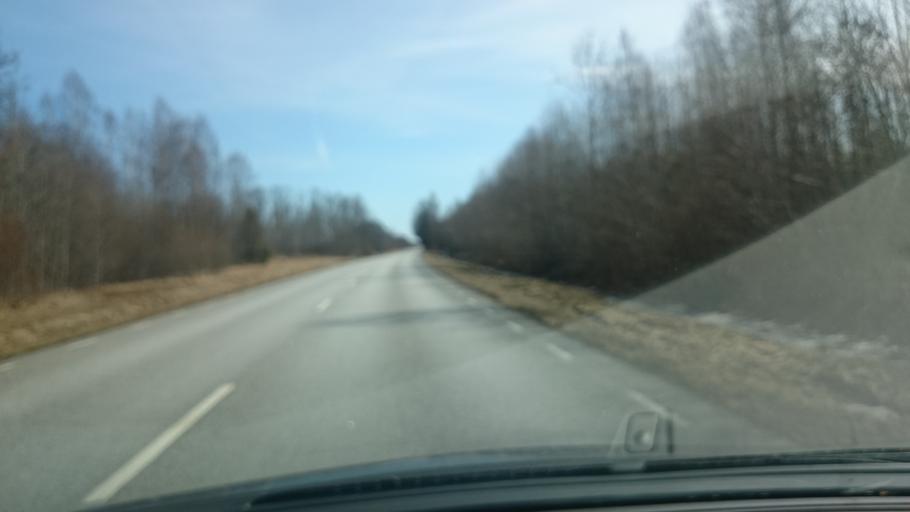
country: EE
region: Paernumaa
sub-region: Tootsi vald
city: Tootsi
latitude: 58.6595
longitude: 24.8285
